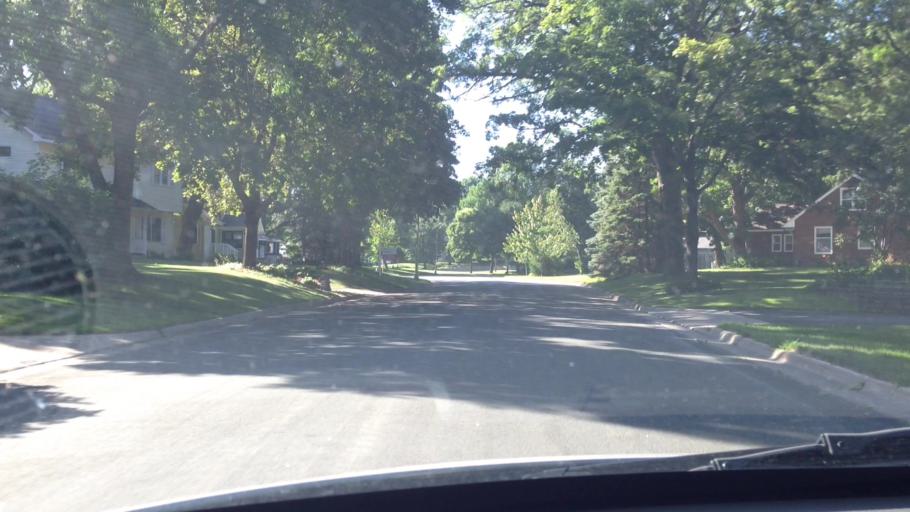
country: US
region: Minnesota
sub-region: Hennepin County
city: Richfield
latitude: 44.8802
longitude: -93.3016
